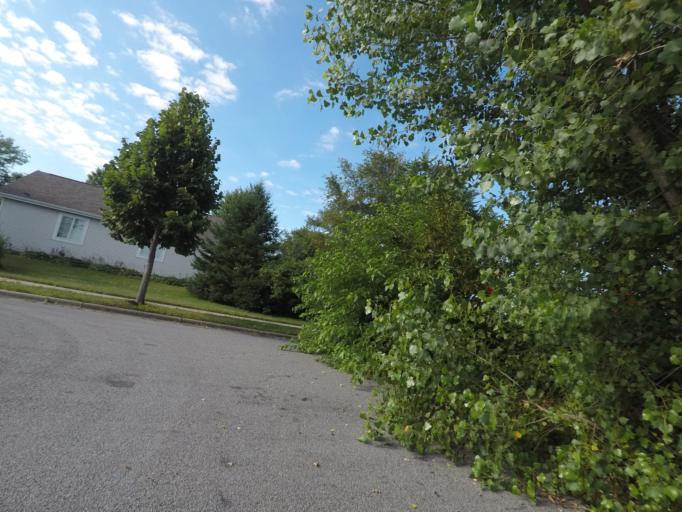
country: US
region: Wisconsin
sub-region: Dane County
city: Middleton
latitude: 43.0709
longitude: -89.5515
